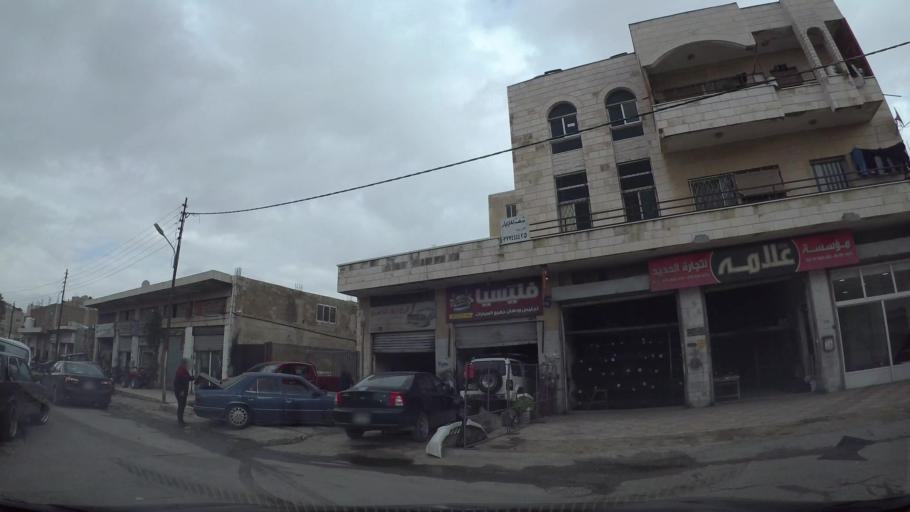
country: JO
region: Amman
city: Wadi as Sir
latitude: 31.9437
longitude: 35.8375
